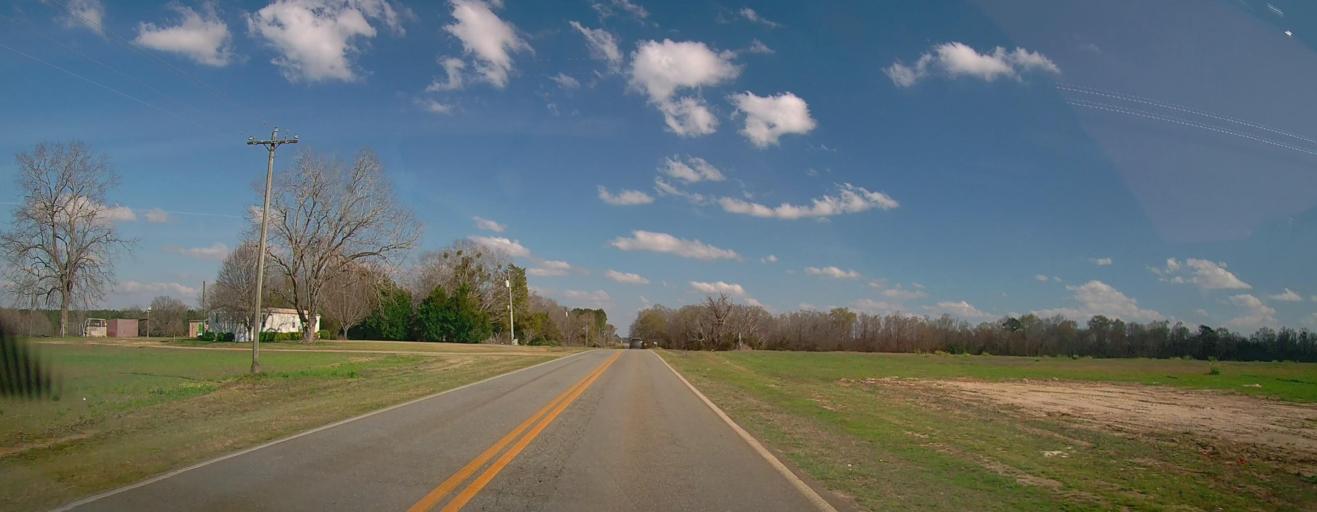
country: US
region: Georgia
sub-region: Laurens County
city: Dublin
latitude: 32.5645
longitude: -83.0215
